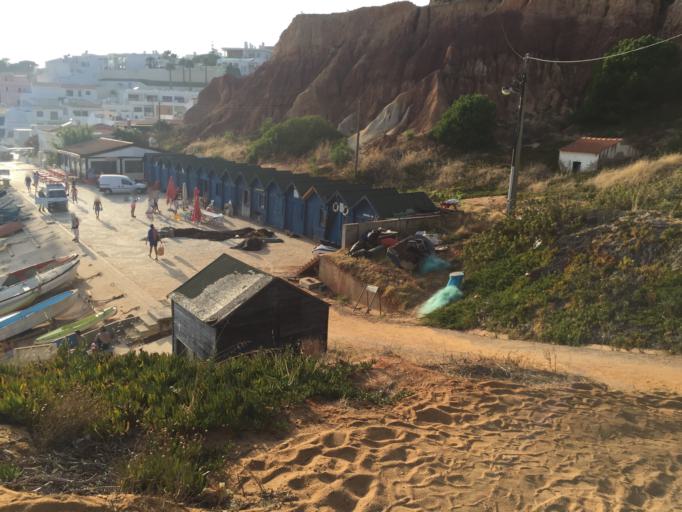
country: PT
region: Faro
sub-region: Loule
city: Boliqueime
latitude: 37.0899
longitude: -8.1888
